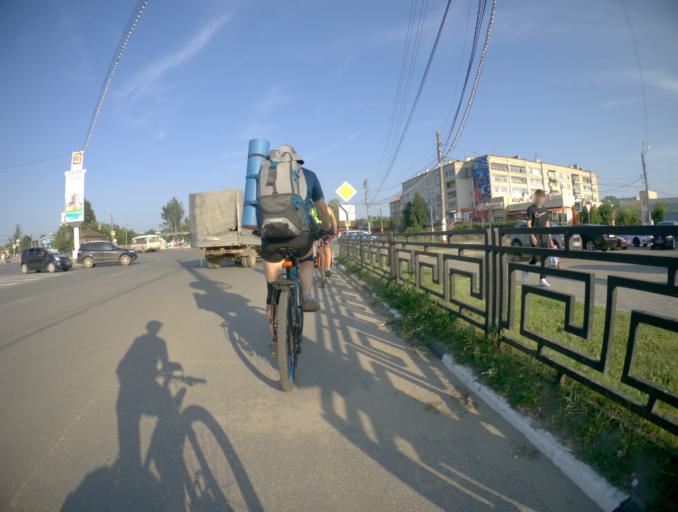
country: RU
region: Nizjnij Novgorod
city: Bor
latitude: 56.3603
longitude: 44.0536
